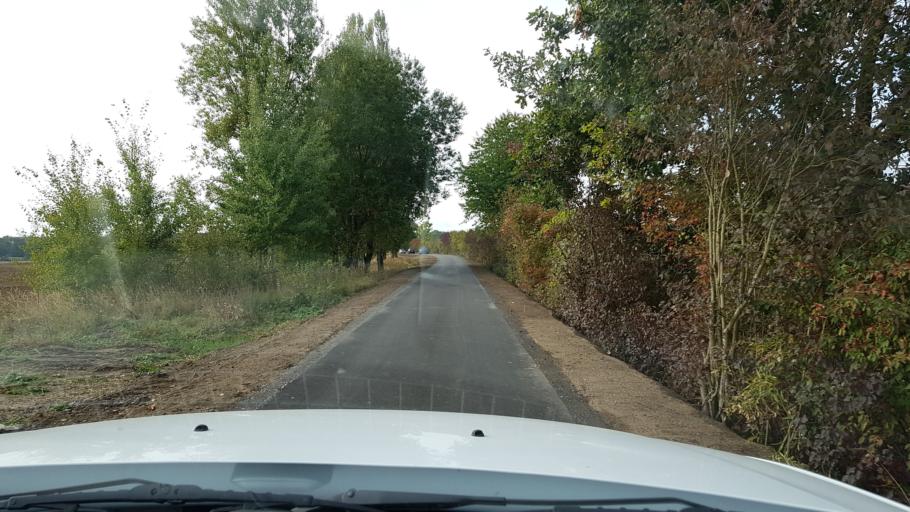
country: PL
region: West Pomeranian Voivodeship
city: Trzcinsko Zdroj
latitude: 52.9381
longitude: 14.5658
